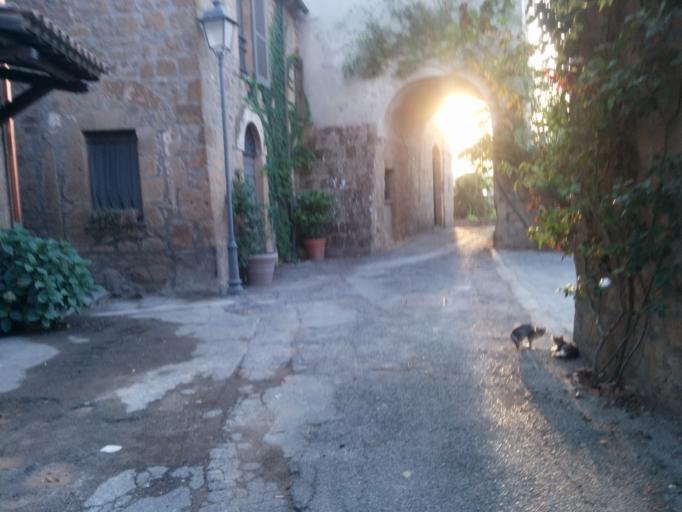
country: IT
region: Umbria
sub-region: Provincia di Terni
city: Sferracavallo
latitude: 42.7222
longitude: 12.0695
